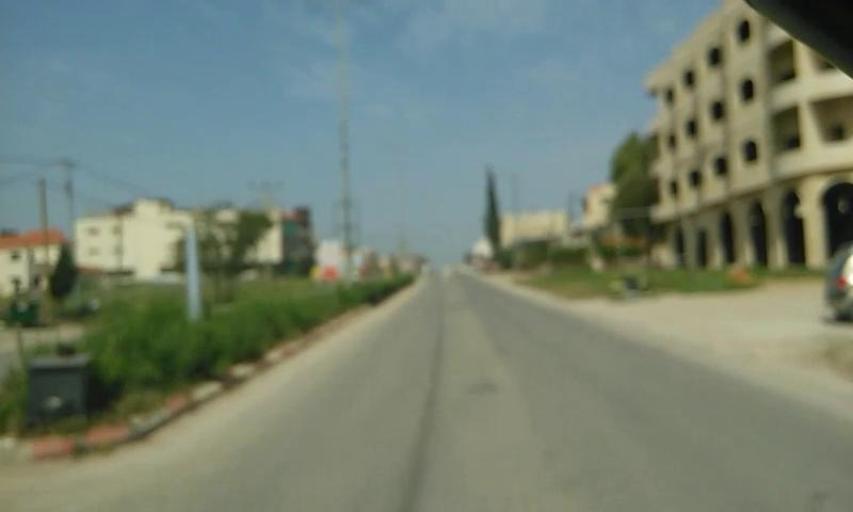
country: PS
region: West Bank
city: Janin
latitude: 32.4829
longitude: 35.2994
